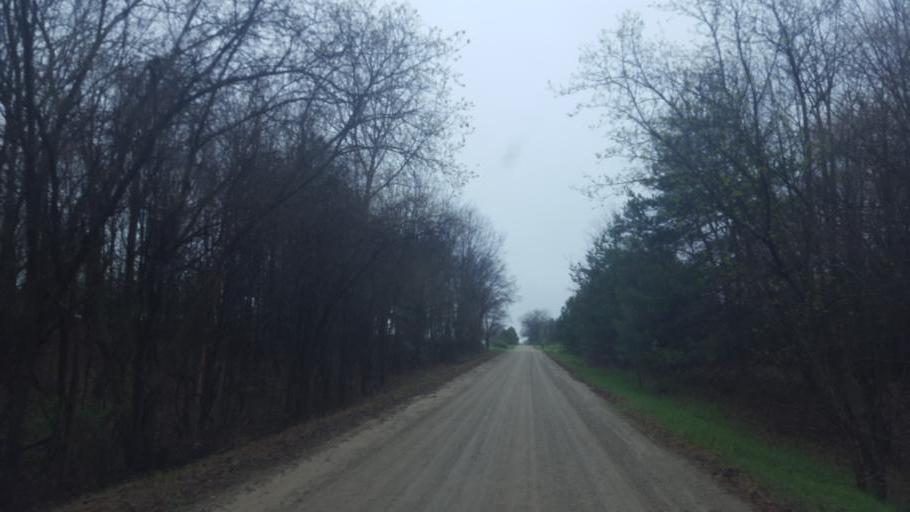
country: US
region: Michigan
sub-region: Isabella County
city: Lake Isabella
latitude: 43.5674
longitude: -84.9990
